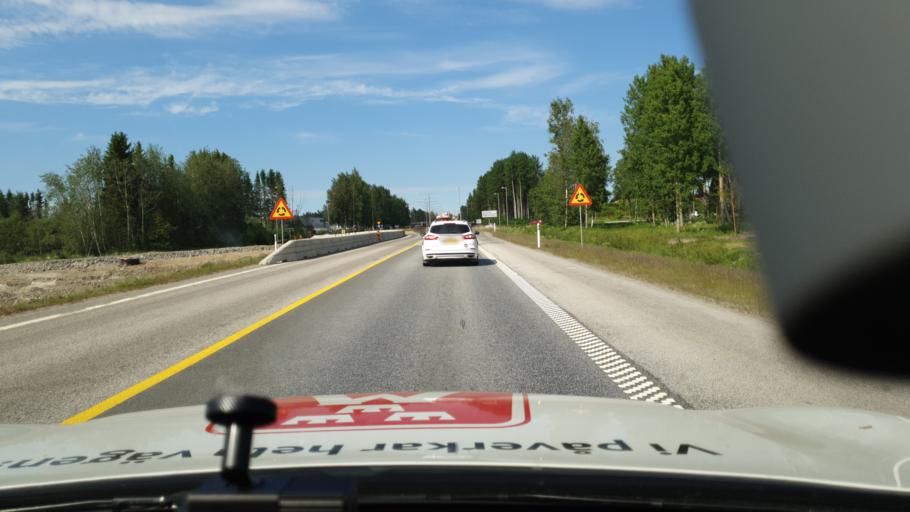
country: SE
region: Vaesterbotten
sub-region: Umea Kommun
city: Umea
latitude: 63.8099
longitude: 20.2492
